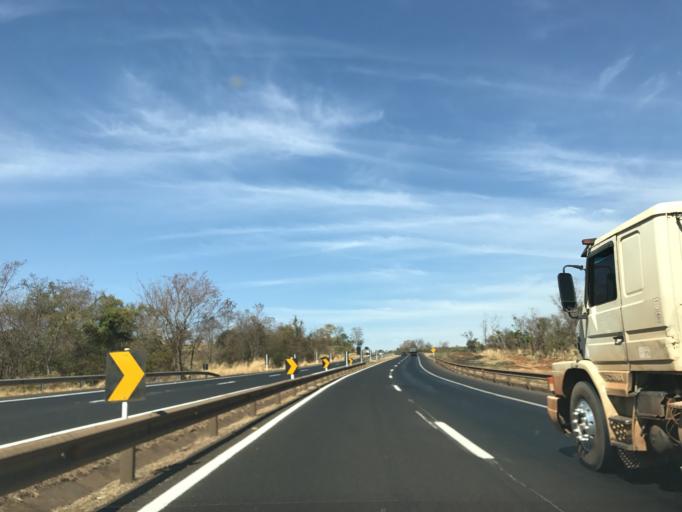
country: BR
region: Minas Gerais
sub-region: Monte Alegre De Minas
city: Monte Alegre de Minas
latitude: -18.8314
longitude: -49.0890
